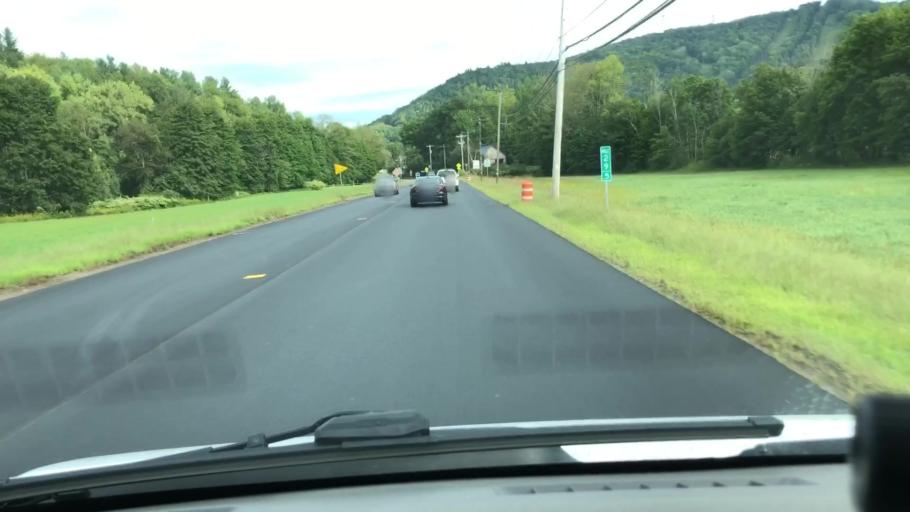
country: US
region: Massachusetts
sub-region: Franklin County
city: Charlemont
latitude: 42.6286
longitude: -72.8882
